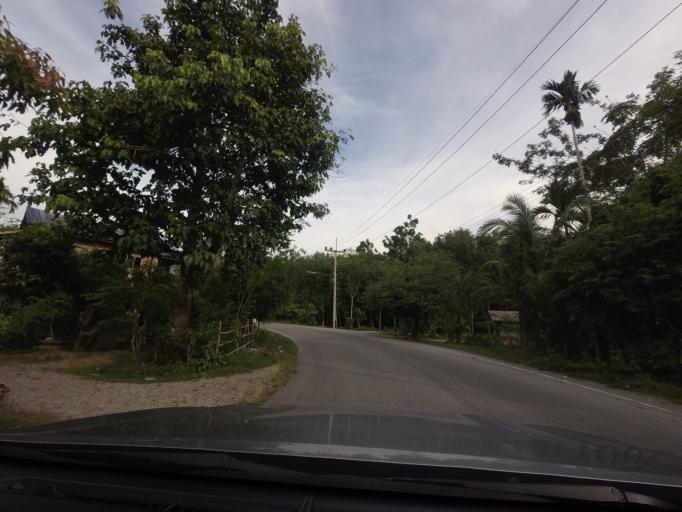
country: TH
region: Narathiwat
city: Rueso
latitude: 6.3473
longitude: 101.4775
